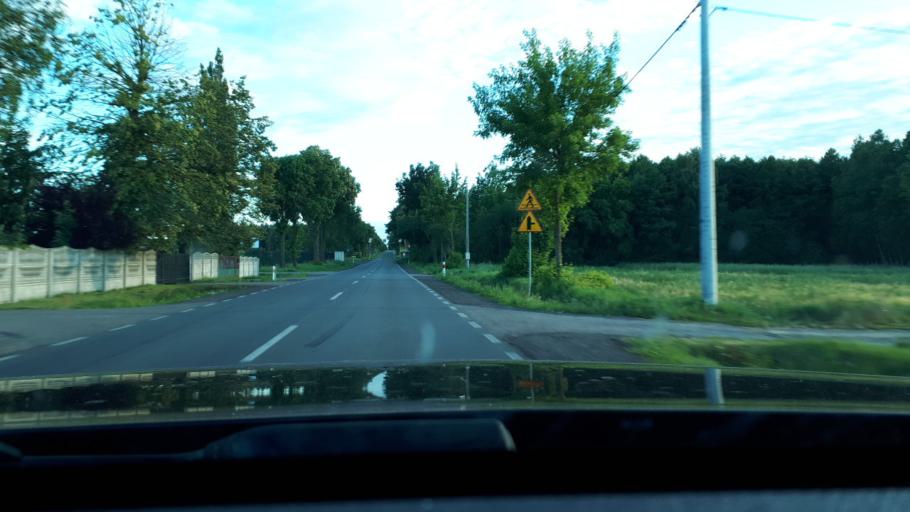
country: PL
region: Masovian Voivodeship
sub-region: Powiat ciechanowski
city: Ojrzen
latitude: 52.7479
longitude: 20.5298
